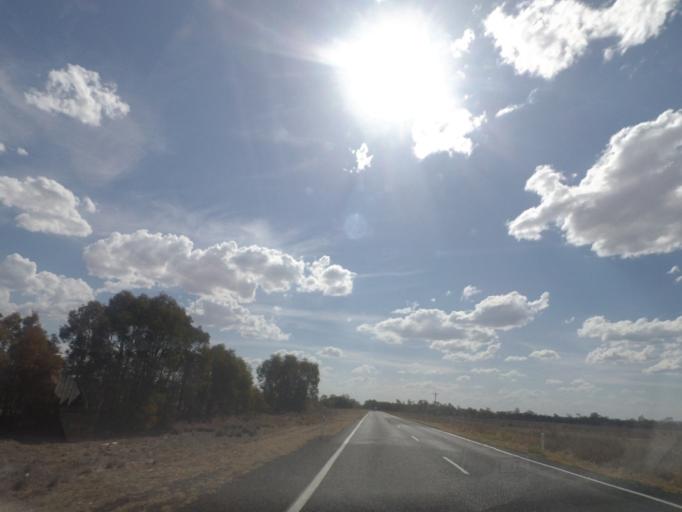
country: AU
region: New South Wales
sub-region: Moree Plains
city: Boggabilla
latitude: -28.4150
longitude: 151.1264
